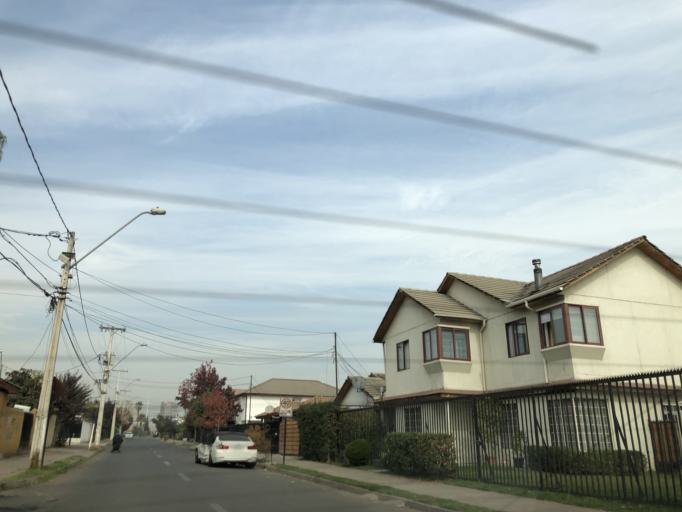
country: CL
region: Santiago Metropolitan
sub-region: Provincia de Cordillera
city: Puente Alto
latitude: -33.5652
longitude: -70.5602
